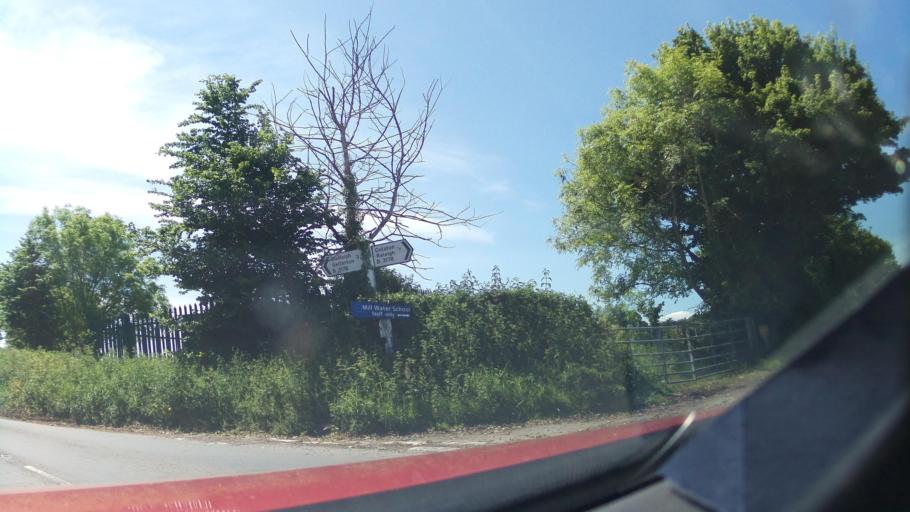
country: GB
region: England
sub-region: Devon
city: Newton Poppleford
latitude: 50.6755
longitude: -3.3103
